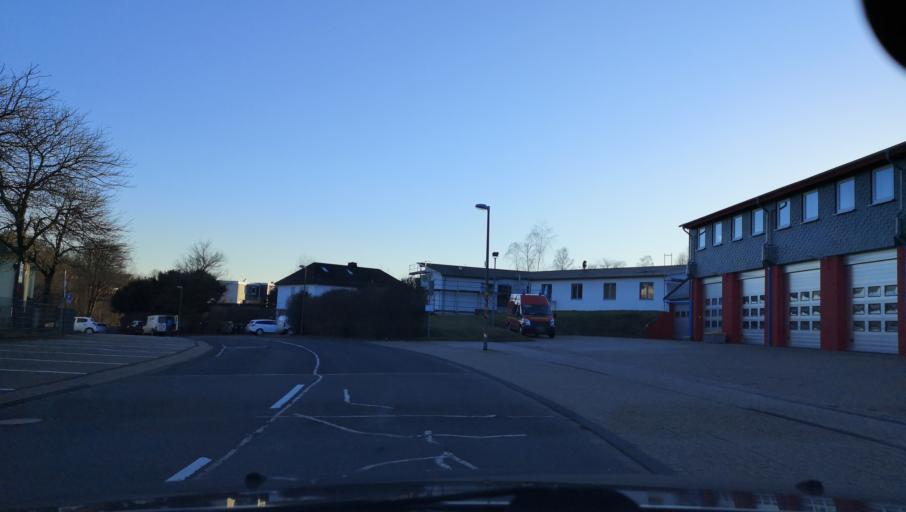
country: DE
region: North Rhine-Westphalia
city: Radevormwald
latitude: 51.1986
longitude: 7.3533
